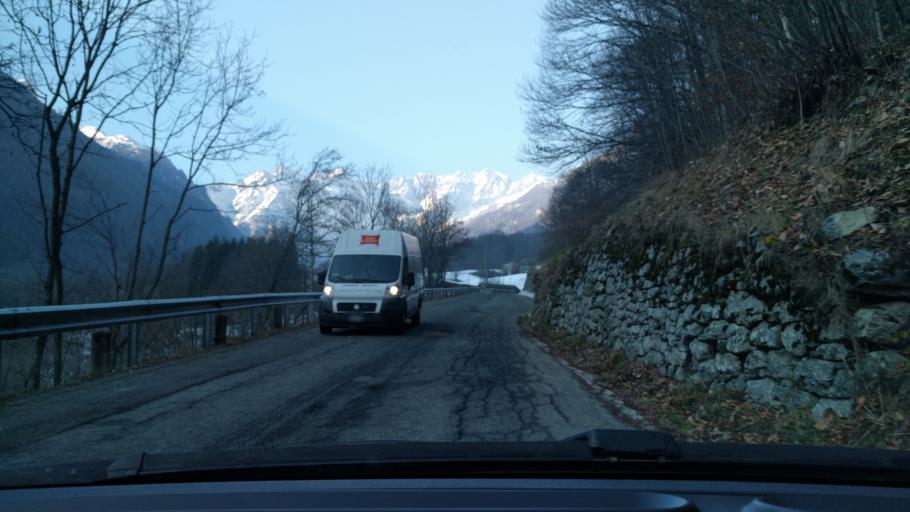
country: IT
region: Piedmont
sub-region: Provincia di Torino
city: Groscavallo
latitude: 45.3697
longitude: 7.2966
